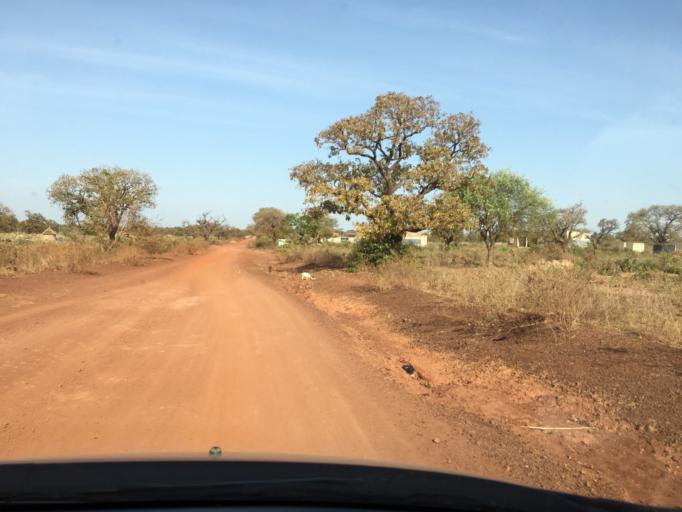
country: BF
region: Plateau-Central
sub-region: Province du Kourweogo
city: Bousse
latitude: 12.5646
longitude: -1.9070
